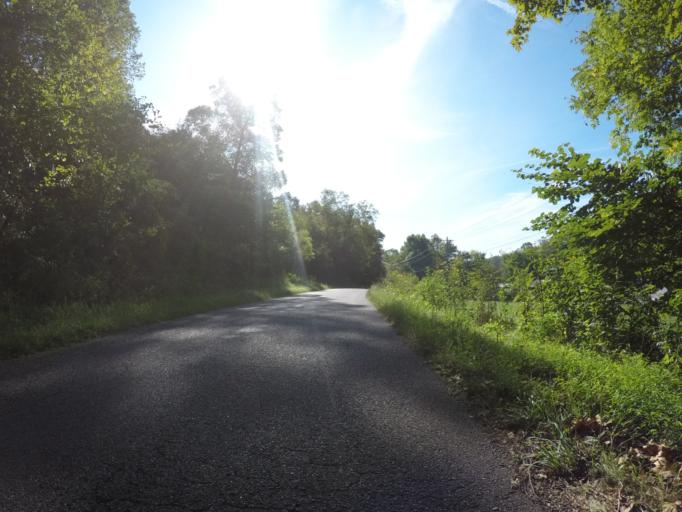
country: US
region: Ohio
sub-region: Lawrence County
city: Burlington
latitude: 38.5042
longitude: -82.5181
